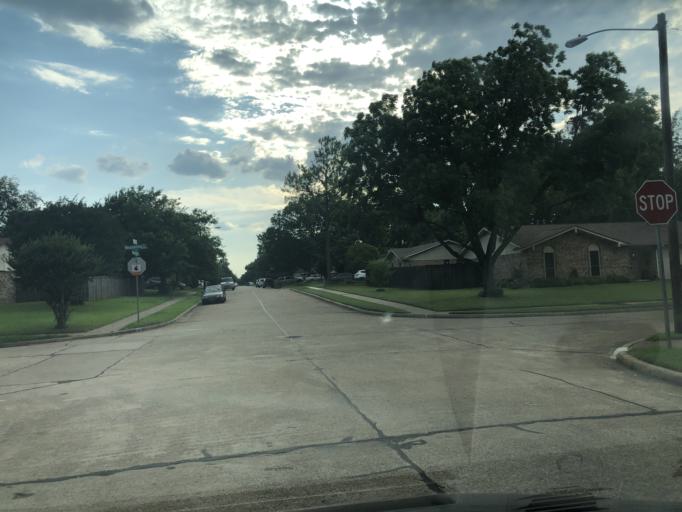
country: US
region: Texas
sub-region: Dallas County
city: Irving
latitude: 32.7891
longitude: -96.9692
